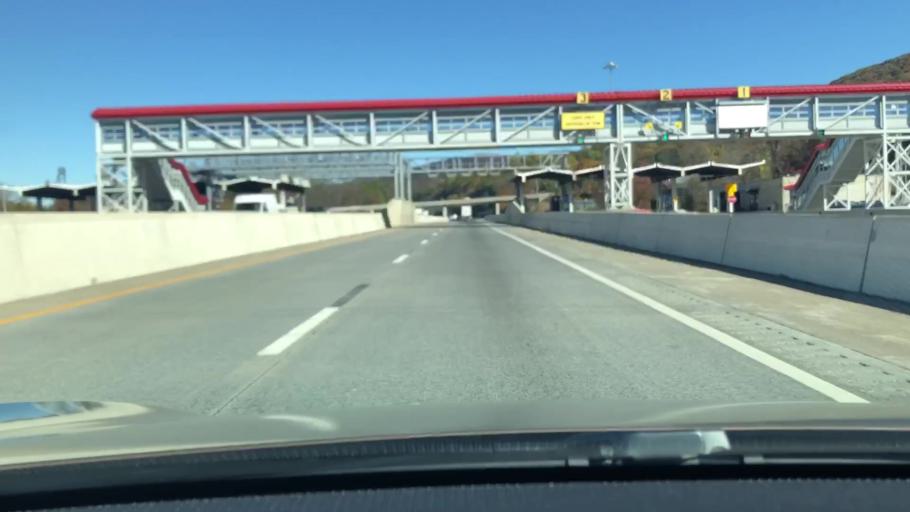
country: US
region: New York
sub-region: Orange County
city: Harriman
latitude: 41.3089
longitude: -74.1254
